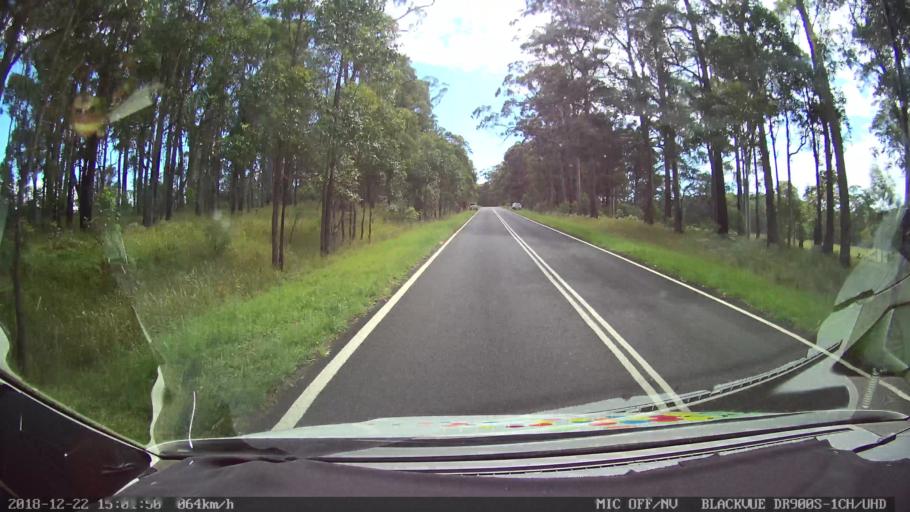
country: AU
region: New South Wales
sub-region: Bellingen
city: Dorrigo
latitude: -30.2582
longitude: 152.4562
